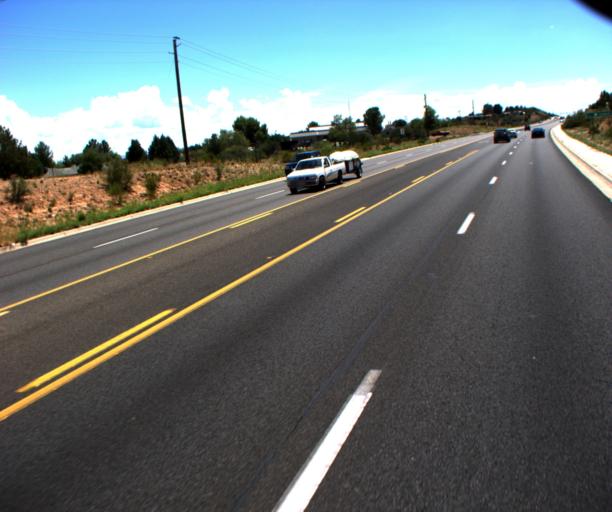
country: US
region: Arizona
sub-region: Yavapai County
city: Verde Village
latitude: 34.7057
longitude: -111.9917
